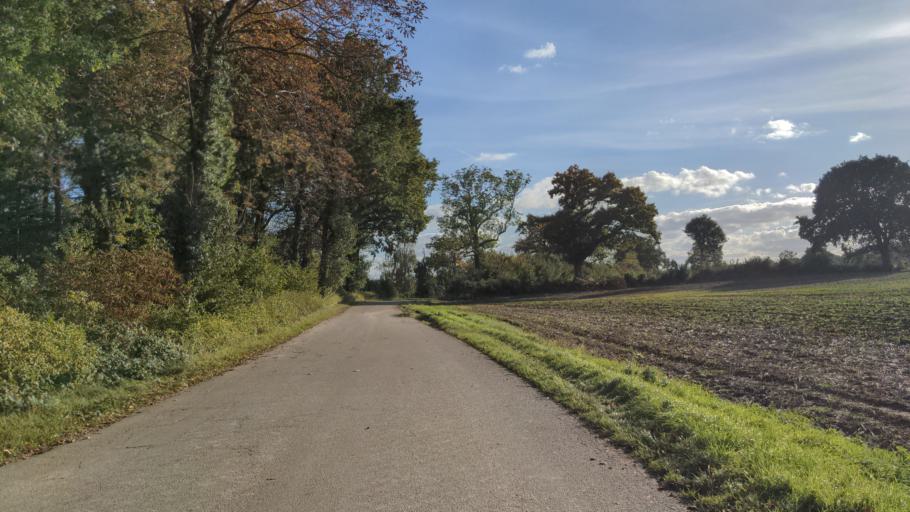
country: DE
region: Schleswig-Holstein
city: Manhagen
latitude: 54.1782
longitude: 10.9155
